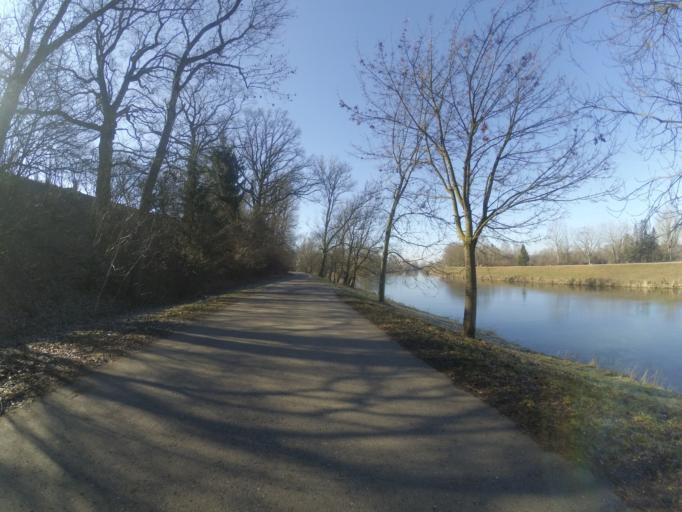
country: DE
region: Baden-Wuerttemberg
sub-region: Tuebingen Region
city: Erbach
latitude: 48.3265
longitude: 9.9267
